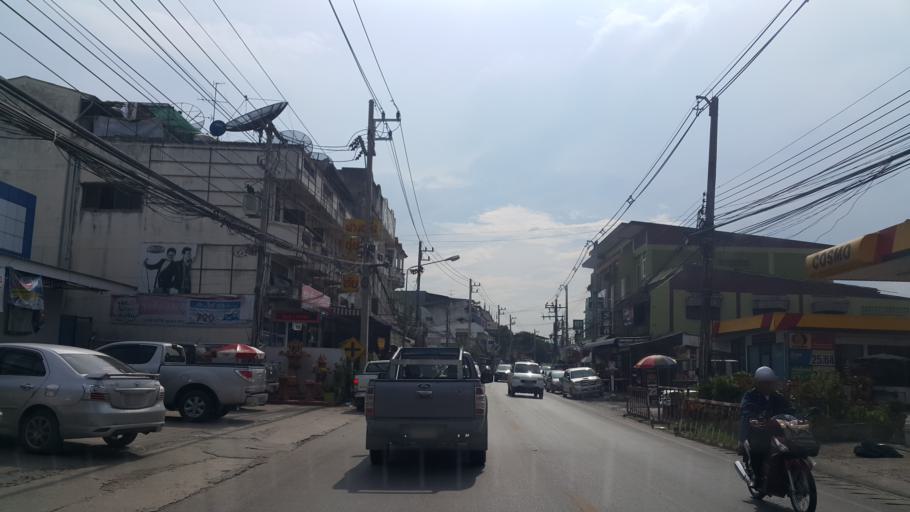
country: TH
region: Chiang Rai
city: Chiang Rai
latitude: 19.8979
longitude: 99.8422
